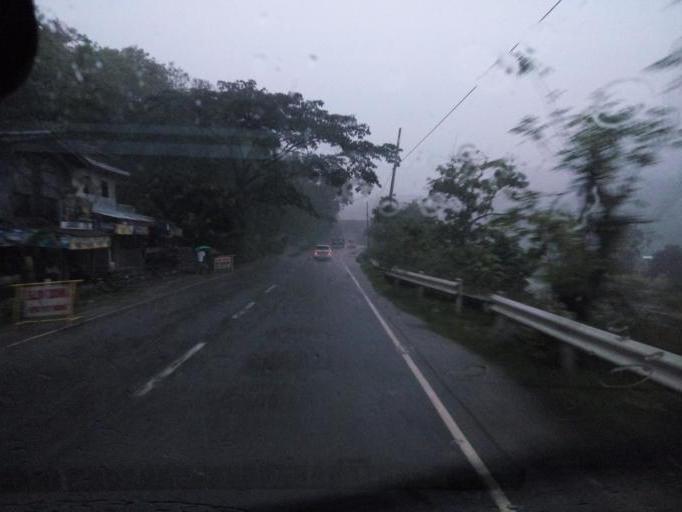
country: PH
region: Cagayan Valley
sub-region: Province of Nueva Vizcaya
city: Santa Fe
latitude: 16.2020
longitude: 120.9512
